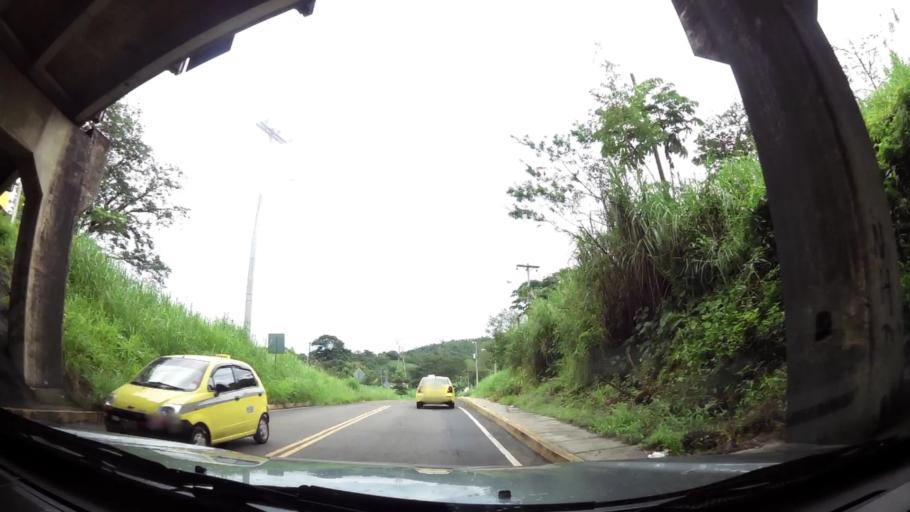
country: PA
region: Panama
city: Chilibre
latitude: 9.1315
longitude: -79.6141
